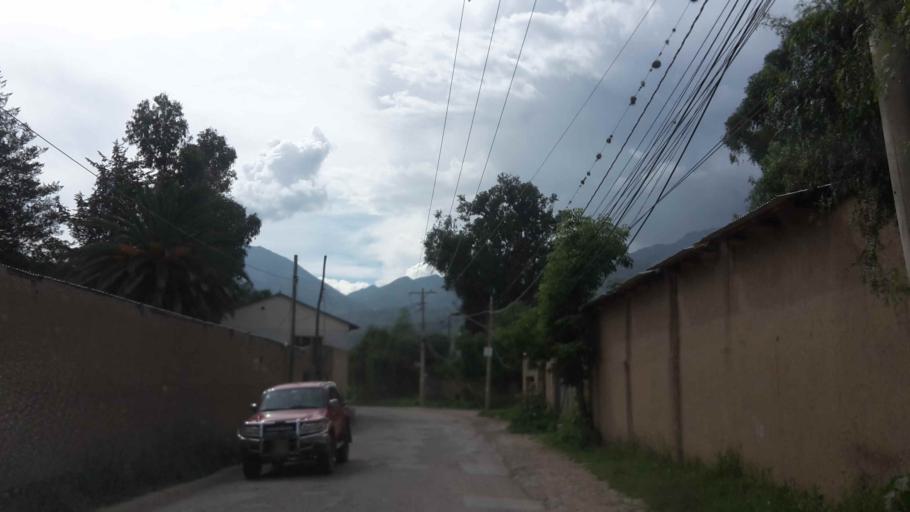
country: BO
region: Cochabamba
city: Cochabamba
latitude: -17.3322
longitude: -66.2379
